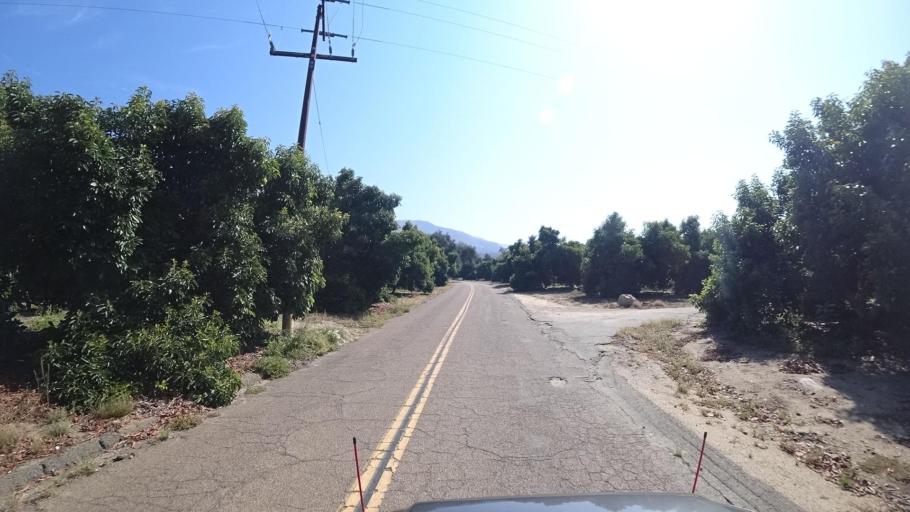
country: US
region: California
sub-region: San Diego County
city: Valley Center
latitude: 33.3201
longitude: -116.9823
